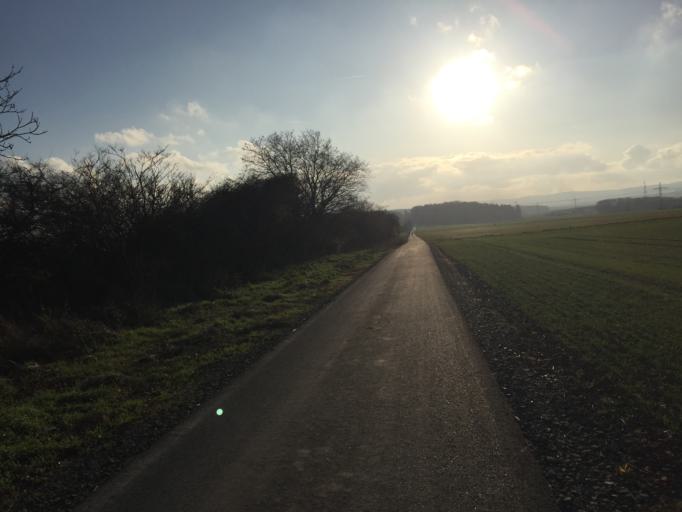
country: DE
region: Hesse
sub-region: Regierungsbezirk Giessen
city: Langgons
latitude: 50.5125
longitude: 8.7092
